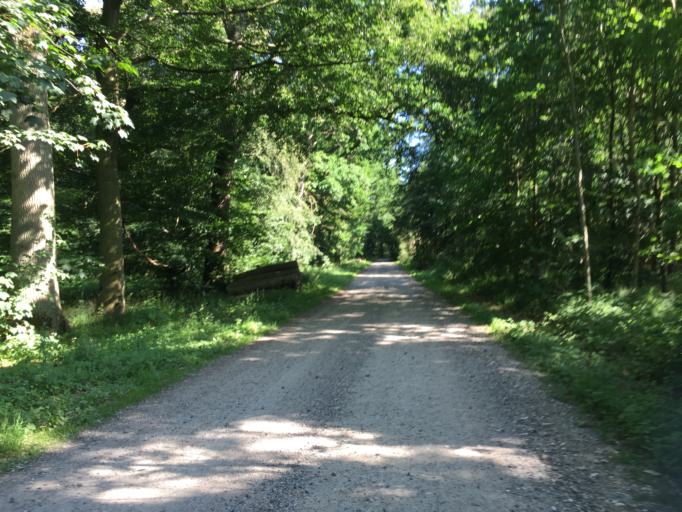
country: DK
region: South Denmark
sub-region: Kerteminde Kommune
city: Langeskov
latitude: 55.3634
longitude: 10.5500
